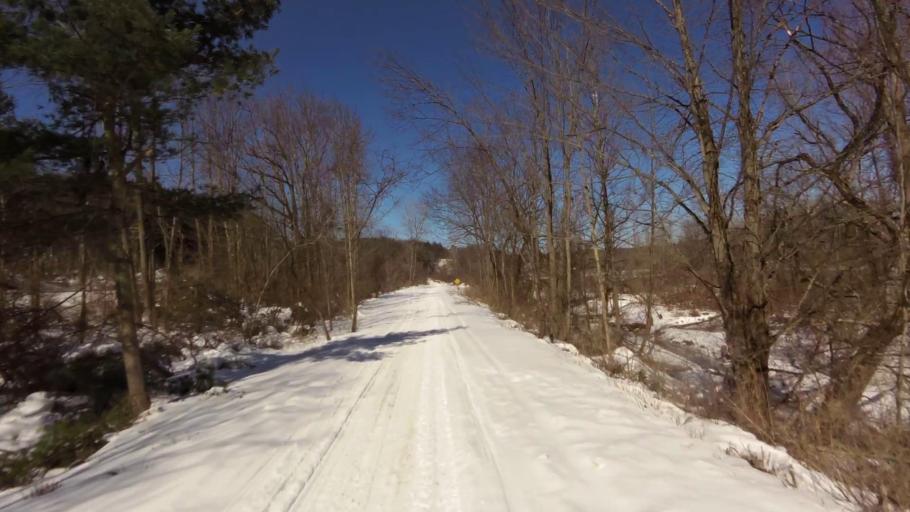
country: US
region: New York
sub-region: Allegany County
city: Houghton
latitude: 42.3783
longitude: -78.1511
